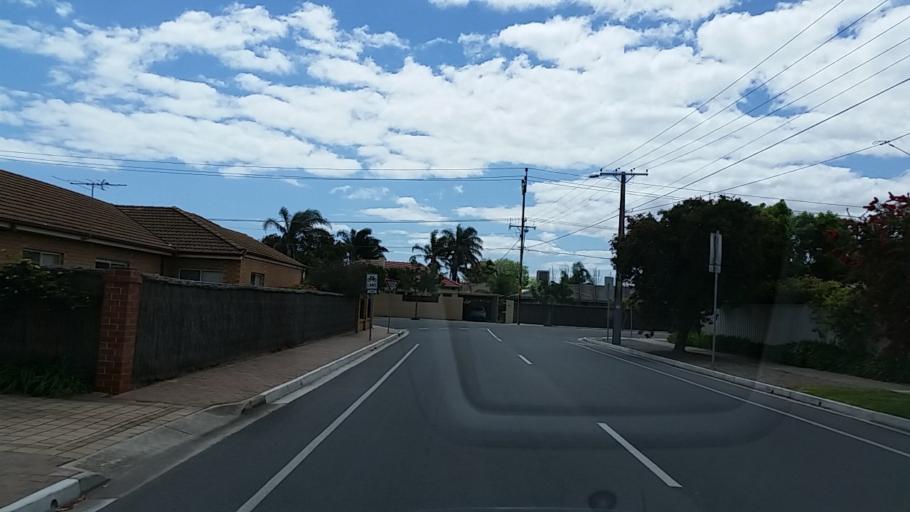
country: AU
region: South Australia
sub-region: Holdfast Bay
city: North Brighton
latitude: -34.9974
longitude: 138.5170
